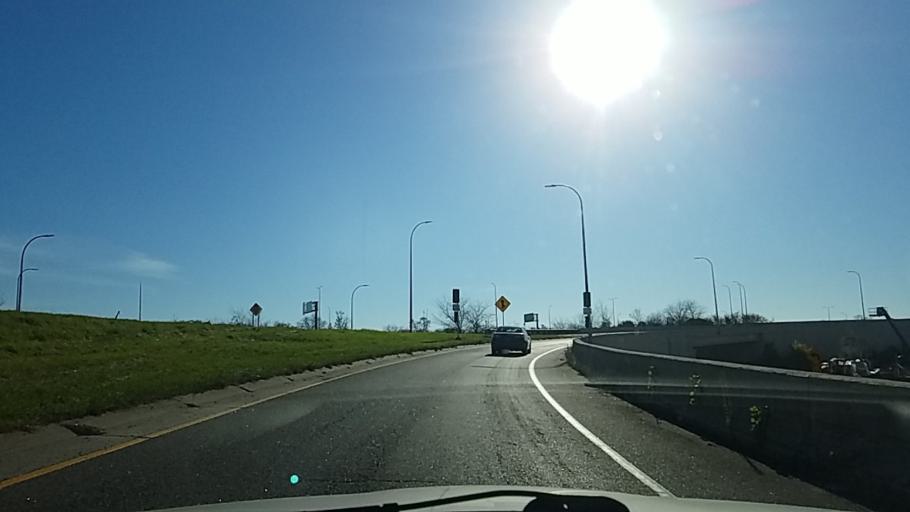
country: US
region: Minnesota
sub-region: Hennepin County
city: Saint Louis Park
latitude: 44.9699
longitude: -93.3436
